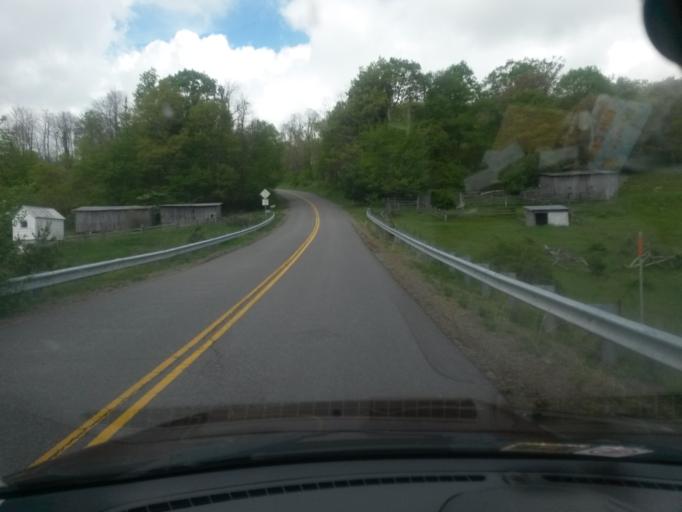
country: US
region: Virginia
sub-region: Floyd County
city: Floyd
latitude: 36.7901
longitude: -80.3877
